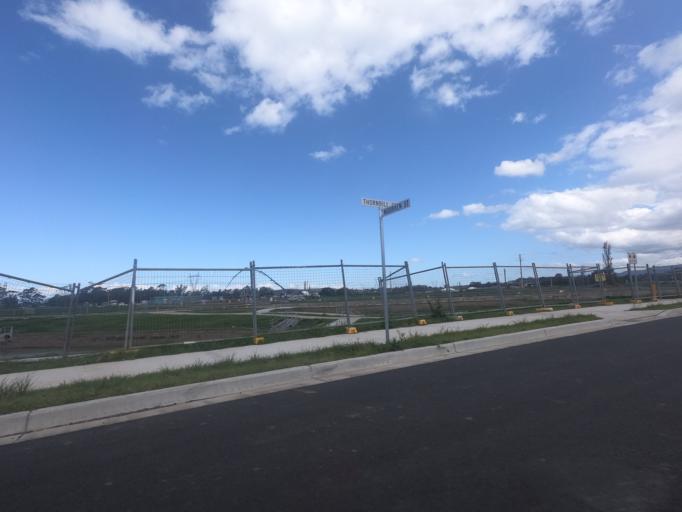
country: AU
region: New South Wales
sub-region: Wollongong
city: Dapto
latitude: -34.4774
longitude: 150.7663
